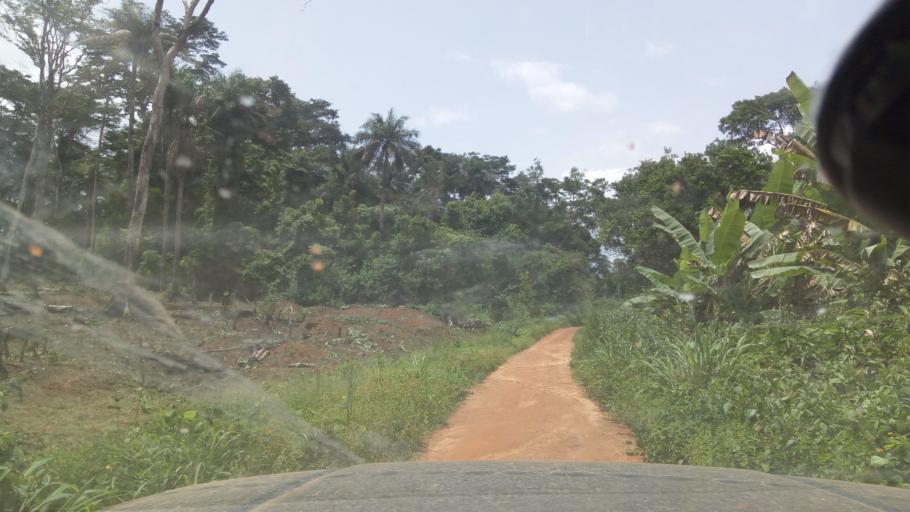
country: SL
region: Eastern Province
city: Giehun
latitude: 7.9640
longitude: -11.0404
